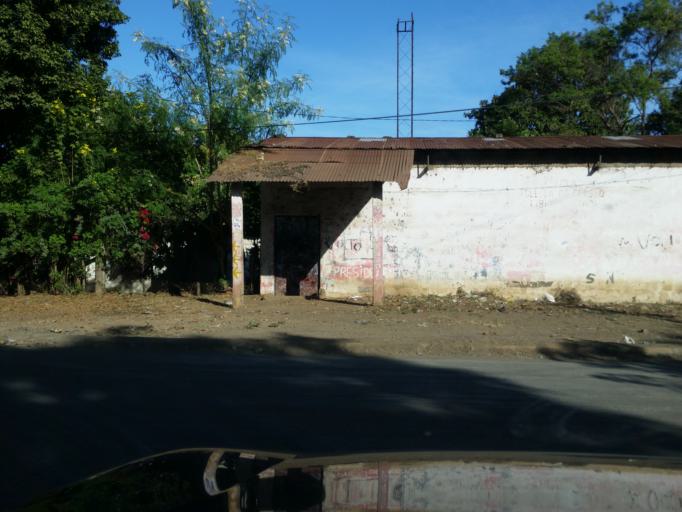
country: NI
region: Masaya
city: Ticuantepe
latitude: 12.0661
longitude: -86.2300
